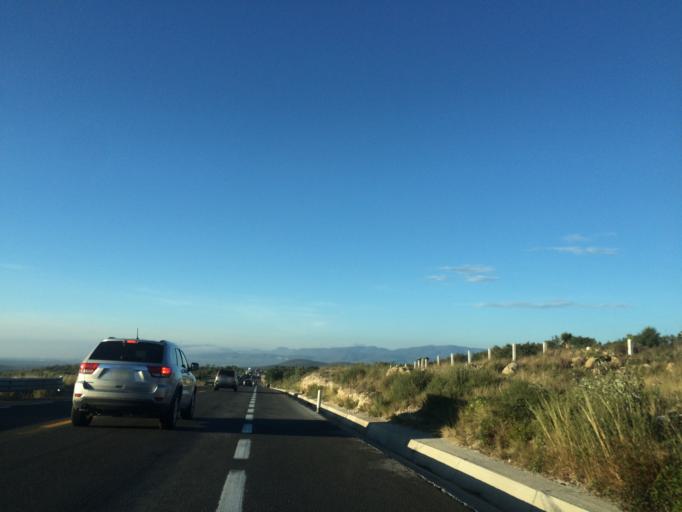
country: MX
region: Puebla
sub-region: Tehuacan
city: Magdalena Cuayucatepec
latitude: 18.6092
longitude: -97.4755
